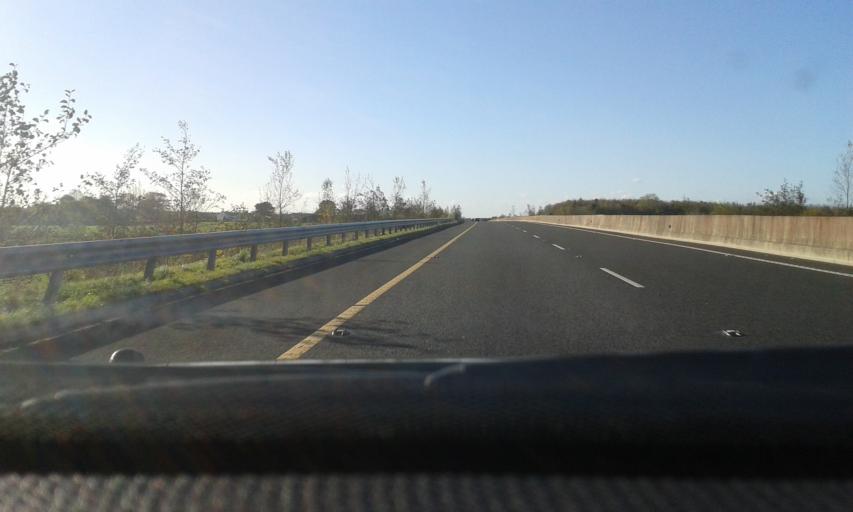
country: IE
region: Munster
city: Thurles
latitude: 52.6929
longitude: -7.6616
